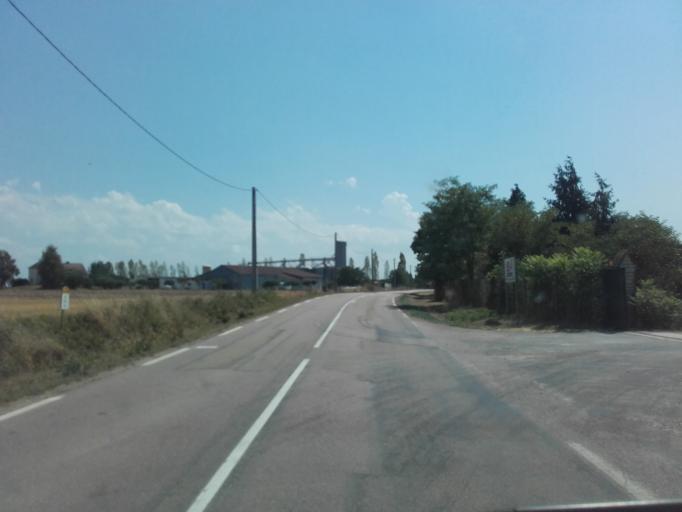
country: FR
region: Bourgogne
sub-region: Departement de l'Yonne
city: Joux-la-Ville
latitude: 47.6672
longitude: 3.8782
